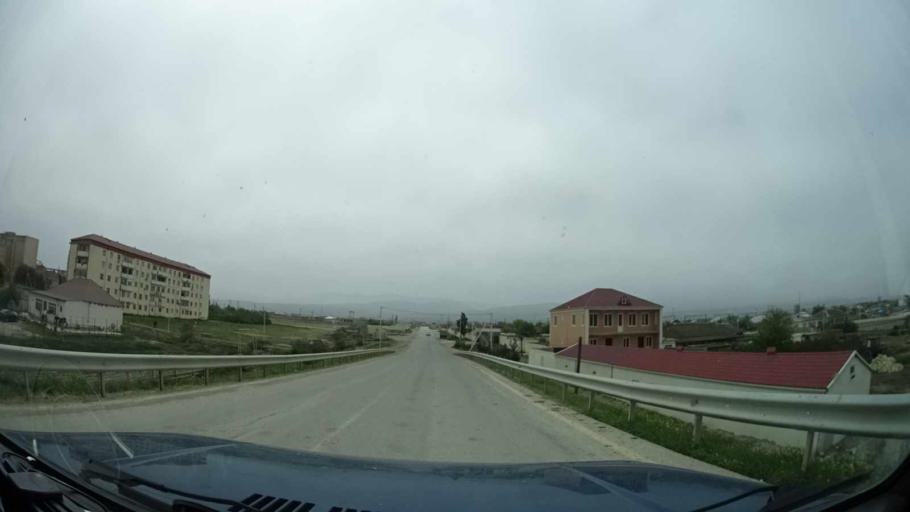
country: AZ
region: Xizi
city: Kilyazi
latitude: 40.8687
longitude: 49.3529
